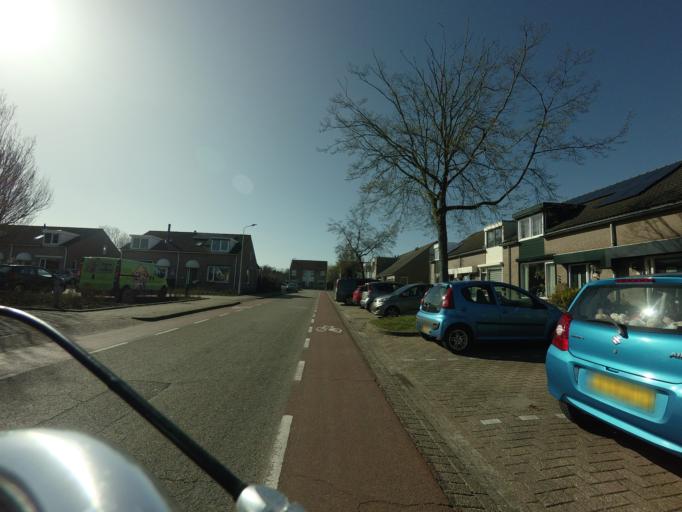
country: NL
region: Zeeland
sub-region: Schouwen-Duiveland
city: Renesse
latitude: 51.7316
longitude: 3.7795
